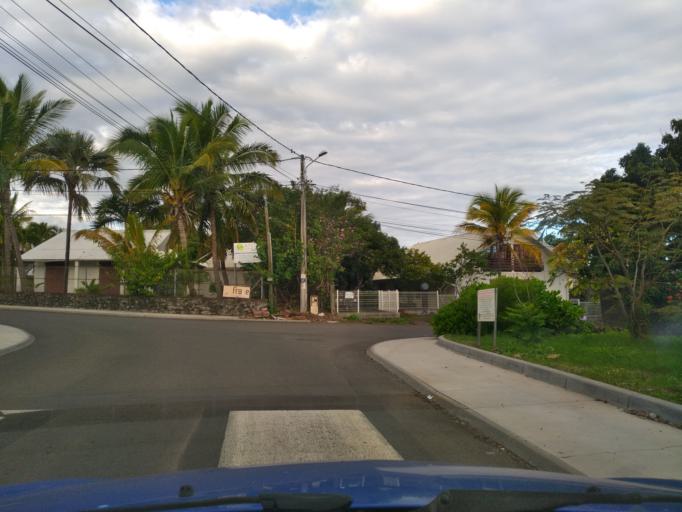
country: RE
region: Reunion
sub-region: Reunion
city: Saint-Pierre
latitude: -21.3300
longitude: 55.4755
